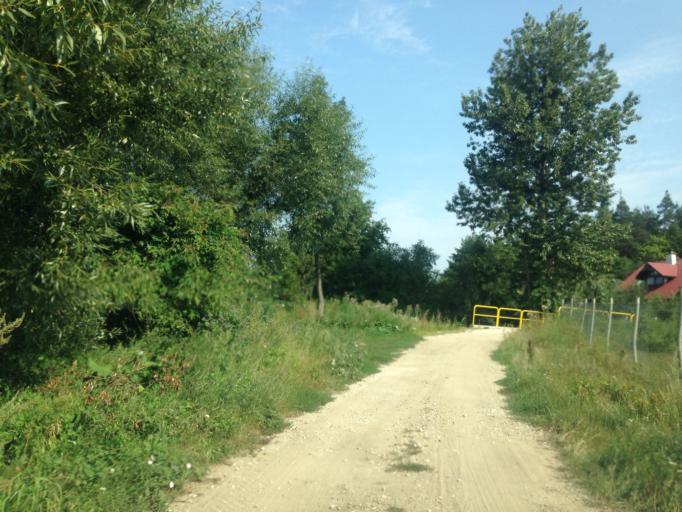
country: PL
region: Kujawsko-Pomorskie
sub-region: Powiat golubsko-dobrzynski
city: Golub-Dobrzyn
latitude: 53.1355
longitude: 19.0951
